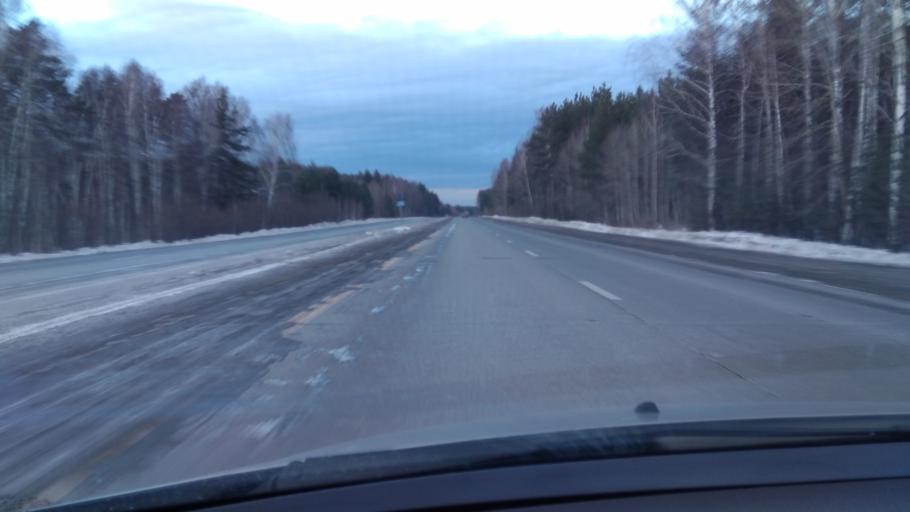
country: RU
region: Sverdlovsk
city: Shchelkun
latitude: 56.3272
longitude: 60.8697
